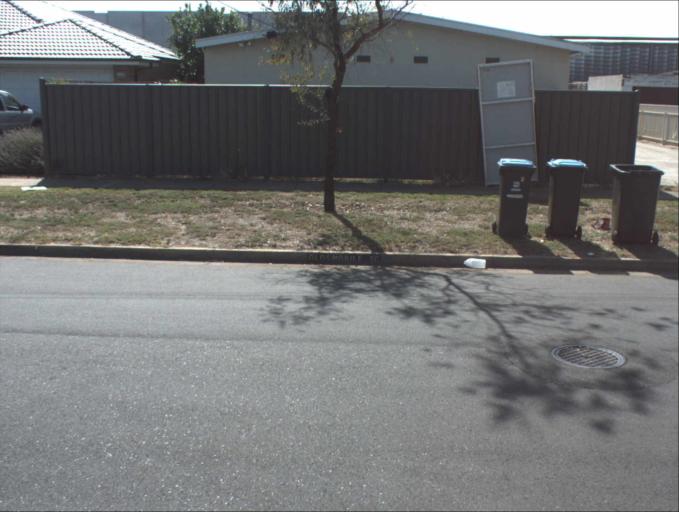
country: AU
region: South Australia
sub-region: Prospect
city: Prospect
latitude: -34.8801
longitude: 138.5769
